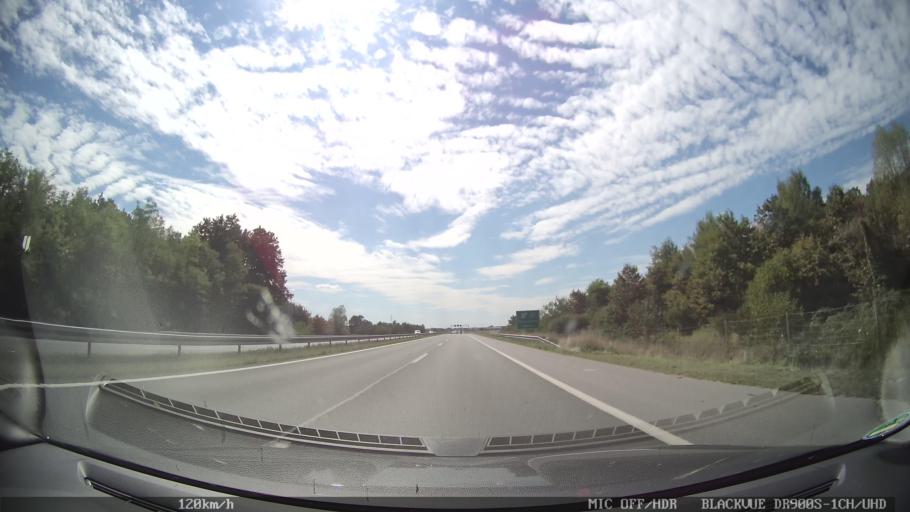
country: HR
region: Grad Zagreb
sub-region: Sesvete
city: Sesvete
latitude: 45.8630
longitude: 16.1748
